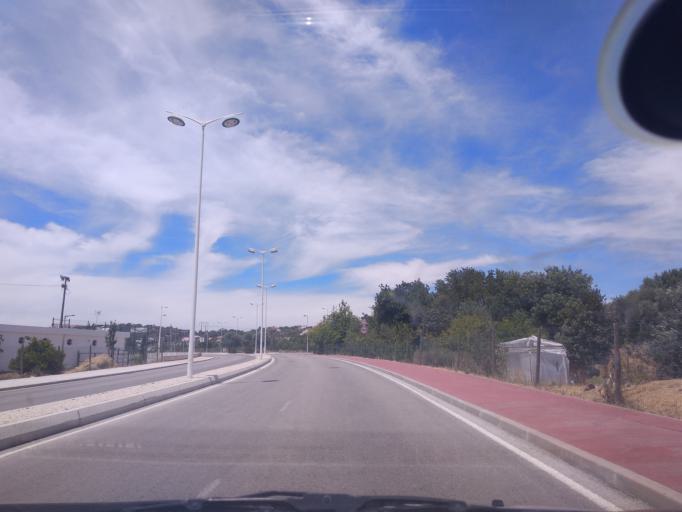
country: PT
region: Faro
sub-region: Sao Bras de Alportel
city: Sao Bras de Alportel
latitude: 37.1574
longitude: -7.8794
